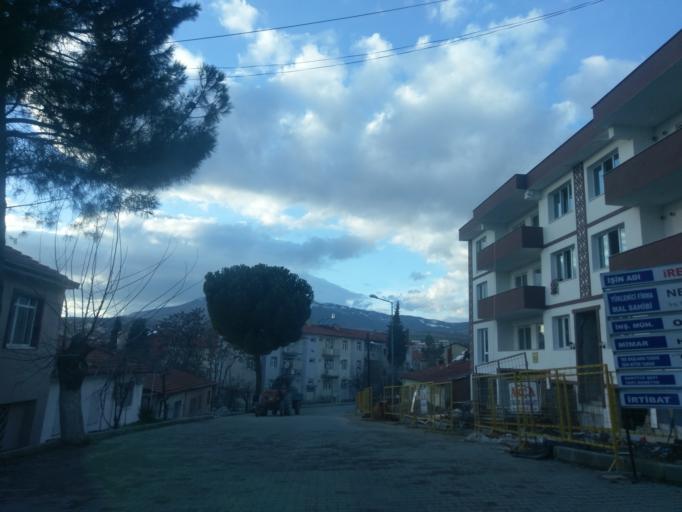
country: TR
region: Kuetahya
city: Gediz
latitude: 38.9924
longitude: 29.3872
